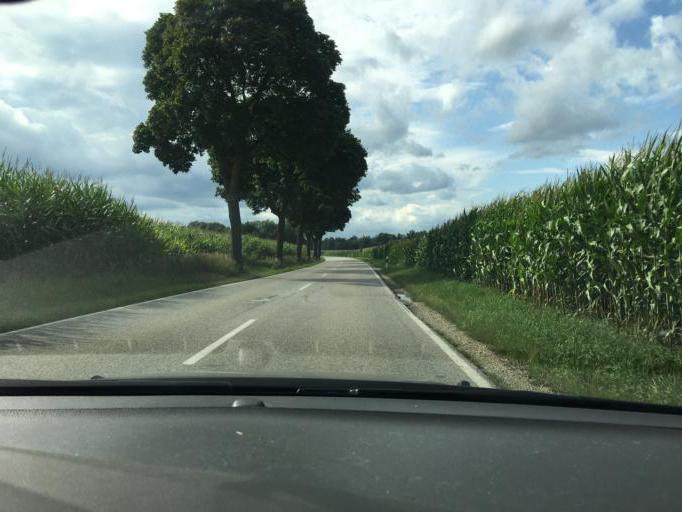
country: DE
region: Bavaria
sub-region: Upper Bavaria
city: Erding
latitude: 48.2986
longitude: 11.9309
